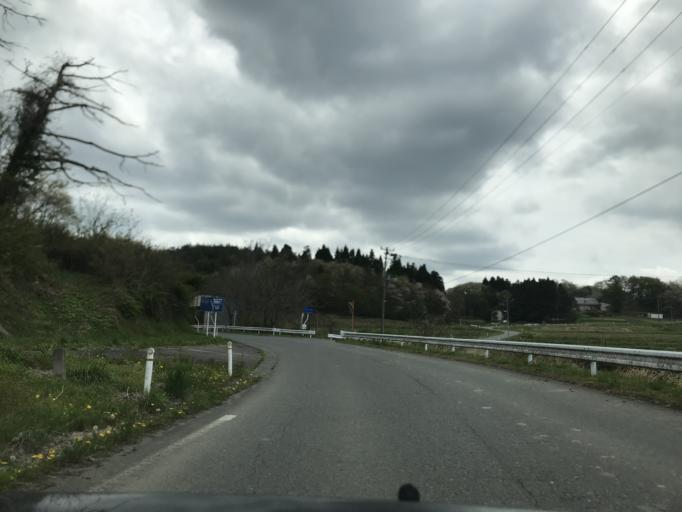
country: JP
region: Iwate
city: Ichinoseki
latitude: 38.8412
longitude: 141.3511
